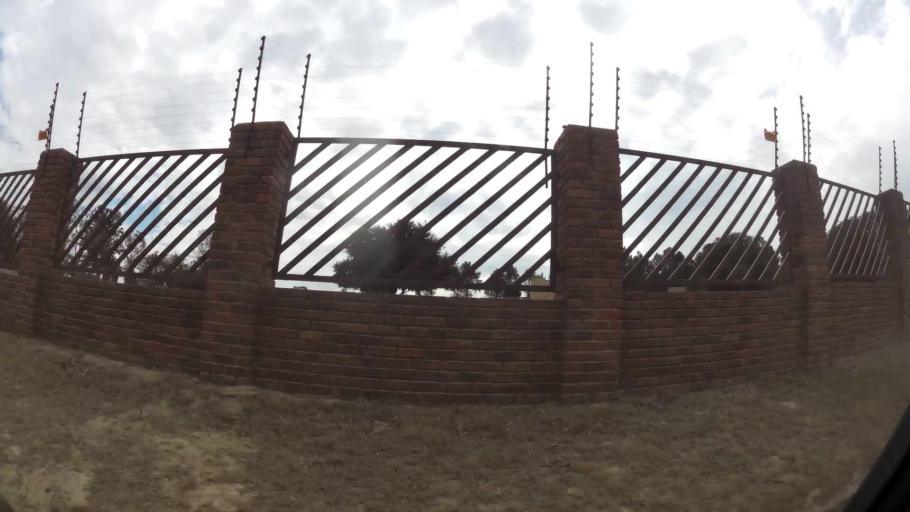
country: ZA
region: Gauteng
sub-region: West Rand District Municipality
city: Muldersdriseloop
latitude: -26.0663
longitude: 27.8906
